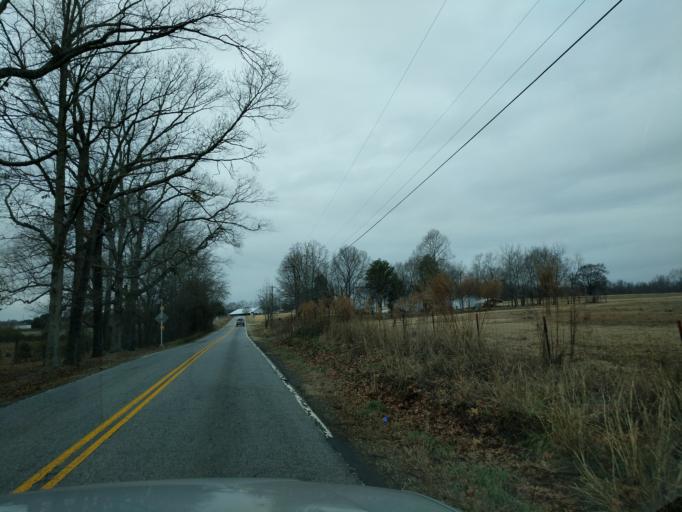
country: US
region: South Carolina
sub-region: Spartanburg County
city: Duncan
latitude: 34.8637
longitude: -82.1173
